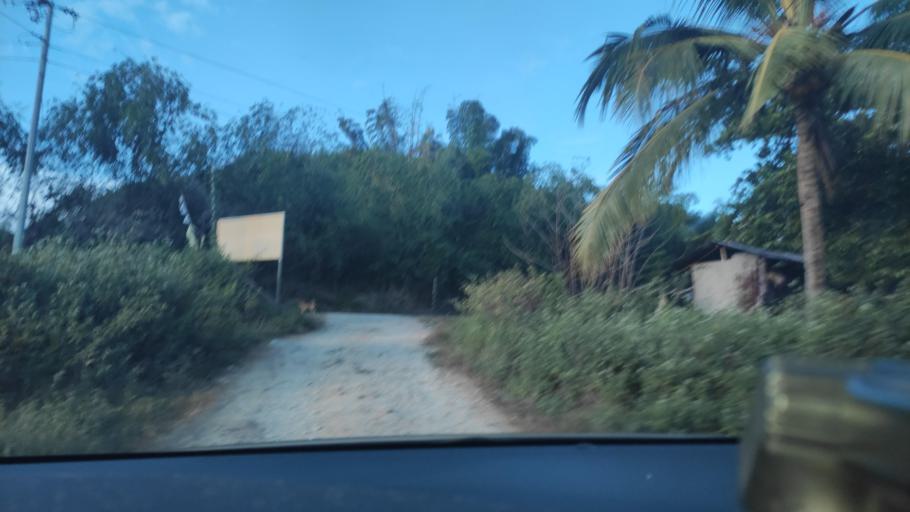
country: PH
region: Ilocos
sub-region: Province of Pangasinan
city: Balingasay
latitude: 16.3063
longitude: 119.8594
